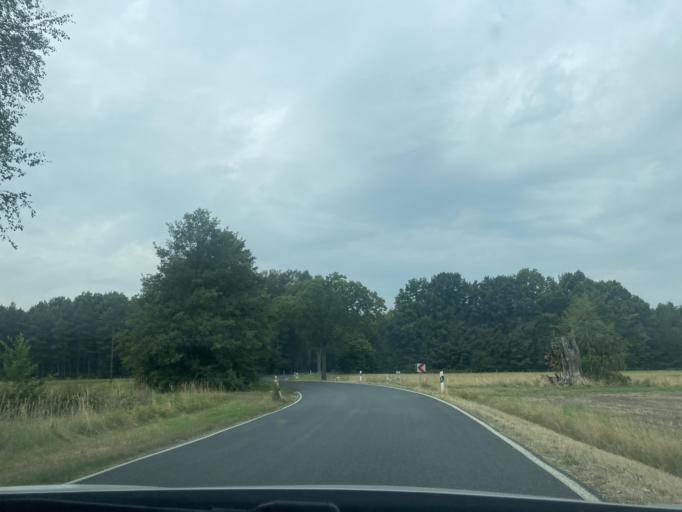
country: DE
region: Saxony
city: Konigswartha
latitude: 51.3056
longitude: 14.3663
